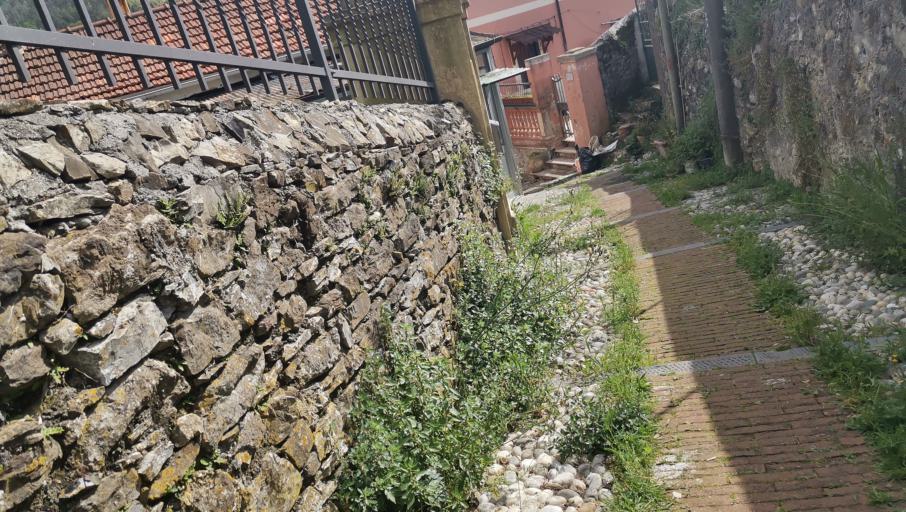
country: IT
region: Liguria
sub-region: Provincia di Genova
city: Piccarello
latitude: 44.4507
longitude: 8.9972
